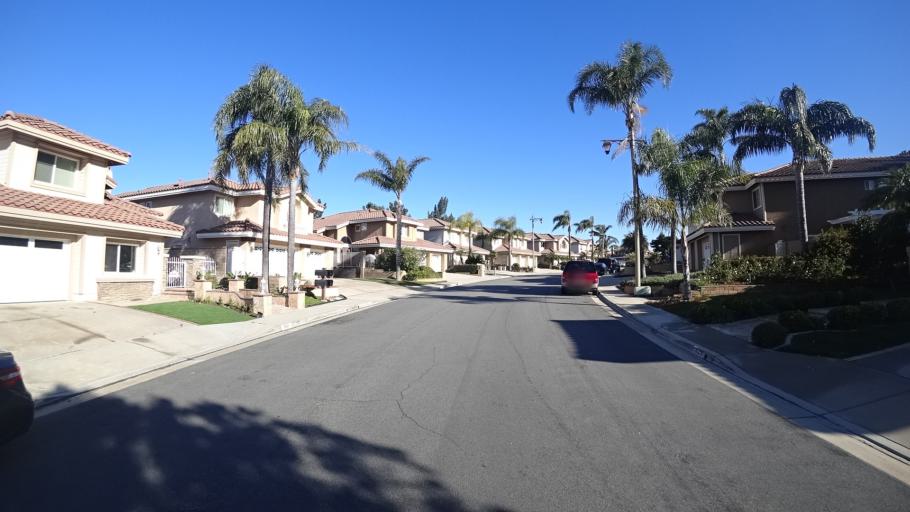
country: US
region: California
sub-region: Orange County
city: Yorba Linda
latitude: 33.8648
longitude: -117.7329
